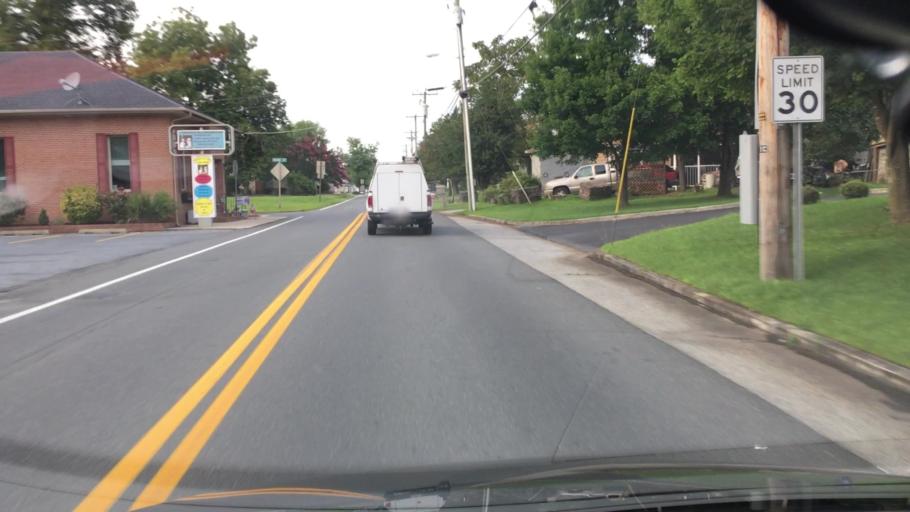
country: US
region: Delaware
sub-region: Sussex County
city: Selbyville
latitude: 38.4432
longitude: -75.1936
